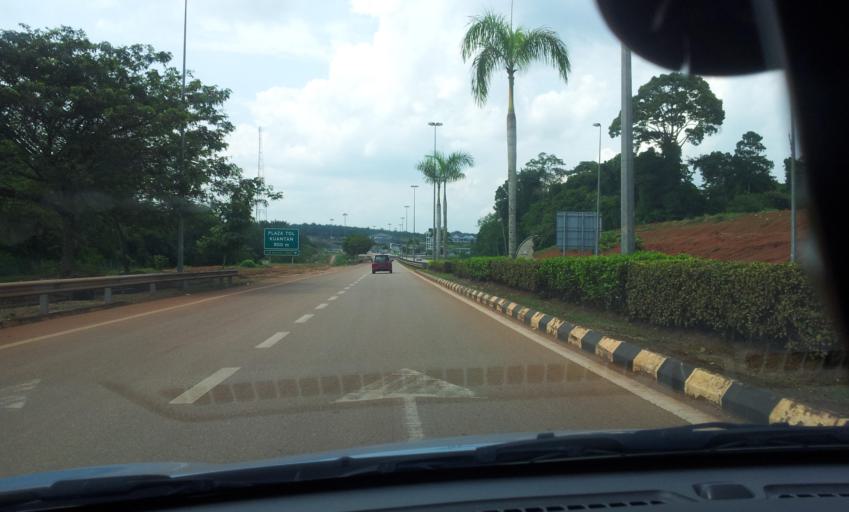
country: MY
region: Pahang
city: Kuantan
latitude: 3.8649
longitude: 103.2394
